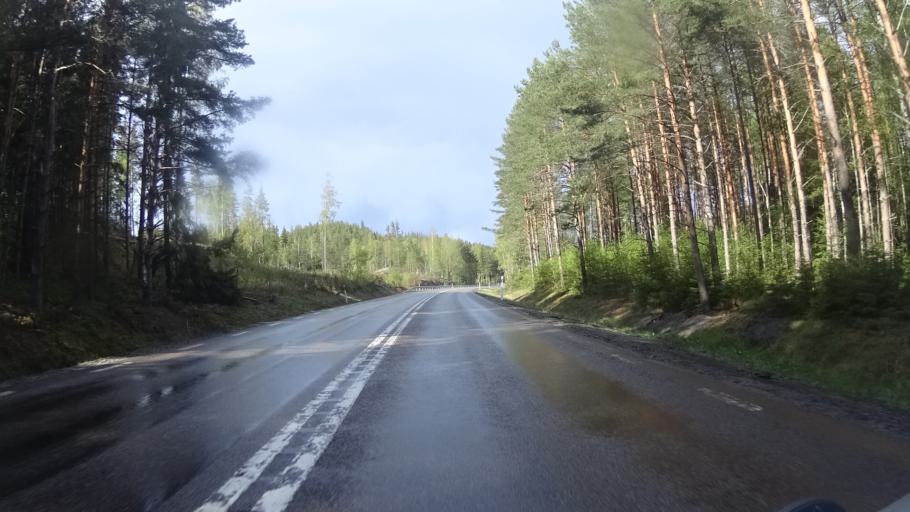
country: SE
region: OErebro
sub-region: Askersunds Kommun
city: Askersund
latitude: 58.7402
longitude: 14.7790
